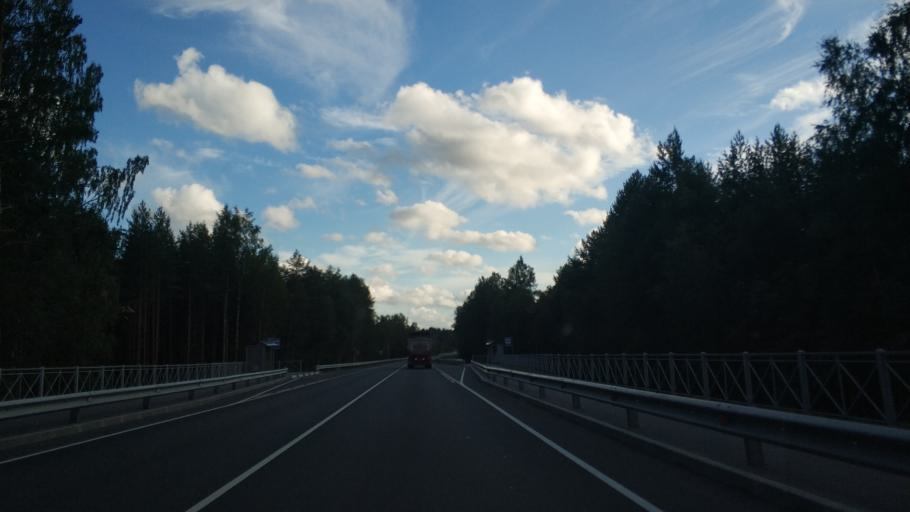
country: RU
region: Leningrad
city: Priozersk
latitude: 60.8661
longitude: 30.1596
